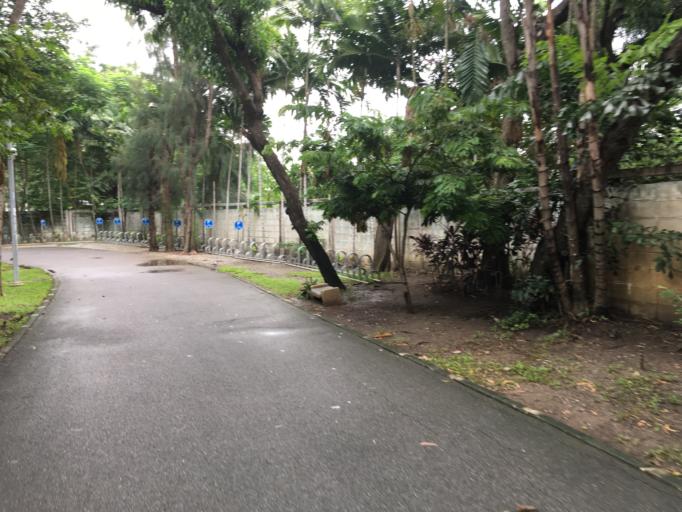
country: TH
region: Bangkok
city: Bueng Kum
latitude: 13.7850
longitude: 100.6731
